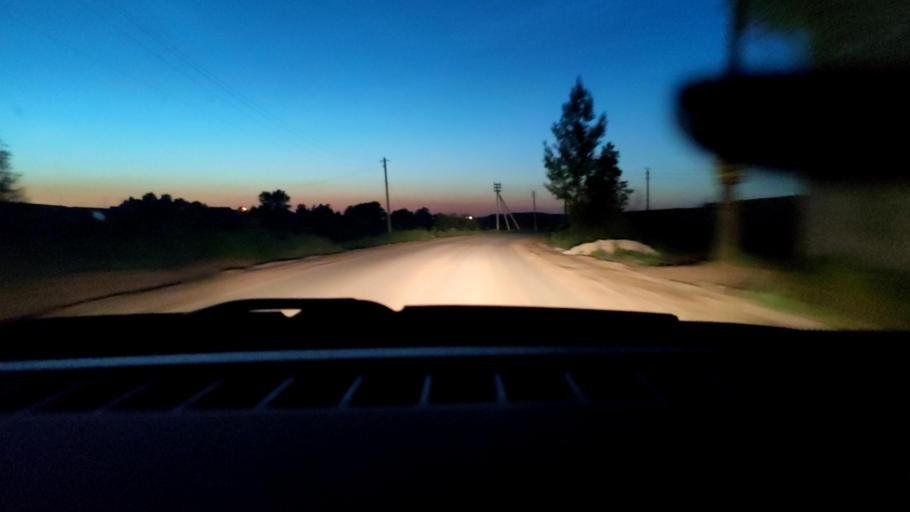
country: RU
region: Perm
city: Kultayevo
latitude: 57.8614
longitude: 55.9824
